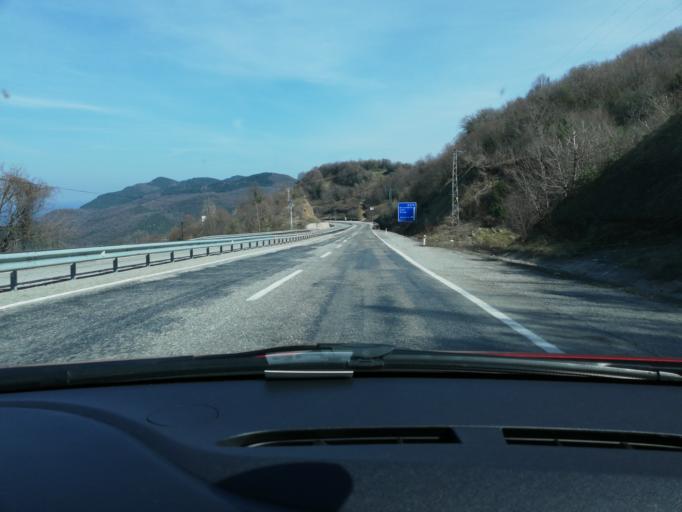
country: TR
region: Bartin
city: Amasra
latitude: 41.7370
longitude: 32.4253
